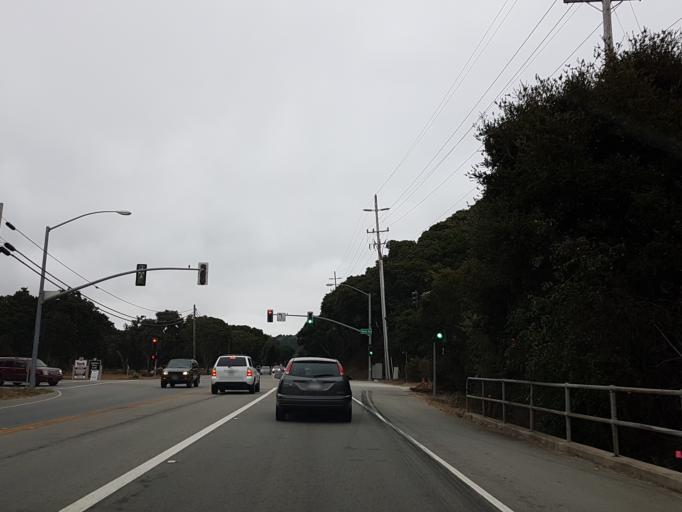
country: US
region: California
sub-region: Monterey County
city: Del Rey Oaks
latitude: 36.5716
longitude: -121.8091
